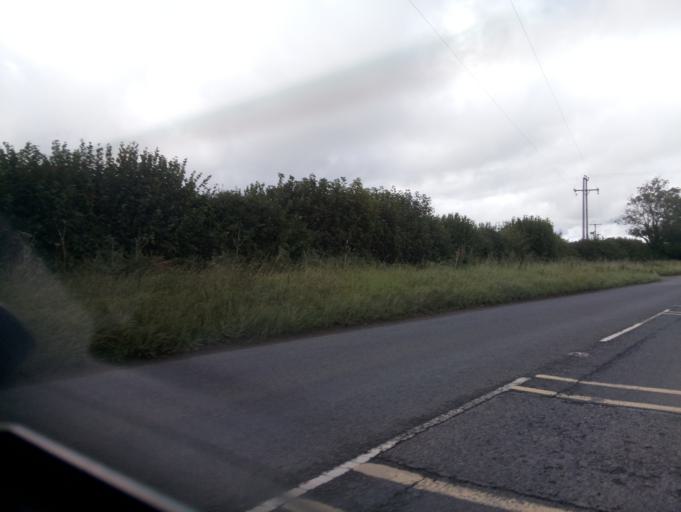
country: GB
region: England
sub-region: Devon
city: Kingsbridge
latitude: 50.3053
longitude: -3.7853
